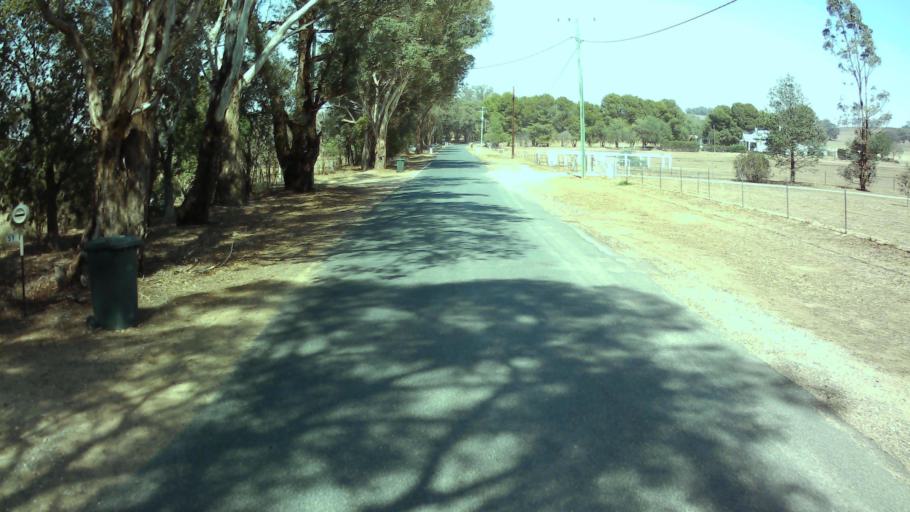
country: AU
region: New South Wales
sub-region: Weddin
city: Grenfell
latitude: -33.8953
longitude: 148.1480
